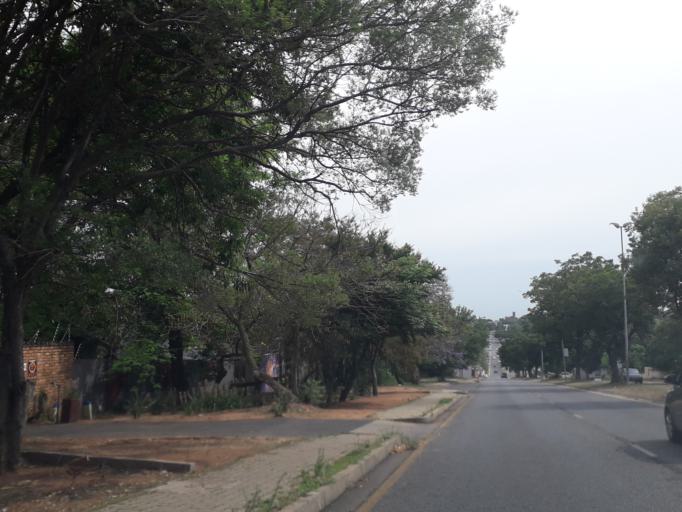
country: ZA
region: Gauteng
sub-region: City of Johannesburg Metropolitan Municipality
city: Roodepoort
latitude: -26.1099
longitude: 27.9735
